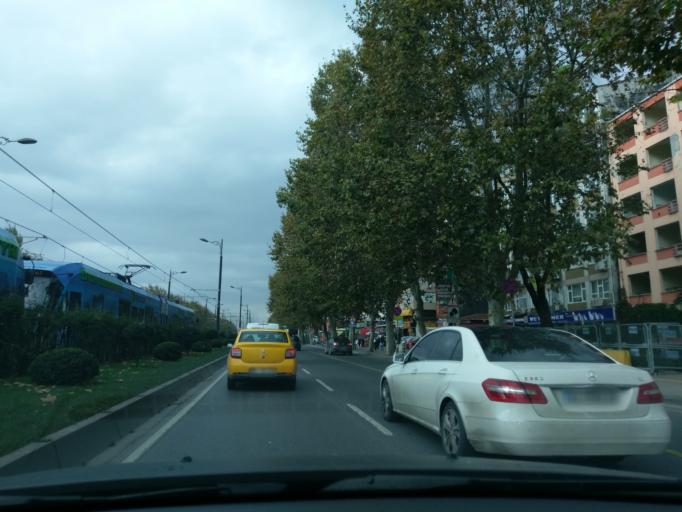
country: TR
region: Istanbul
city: Istanbul
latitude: 41.0170
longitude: 28.9299
